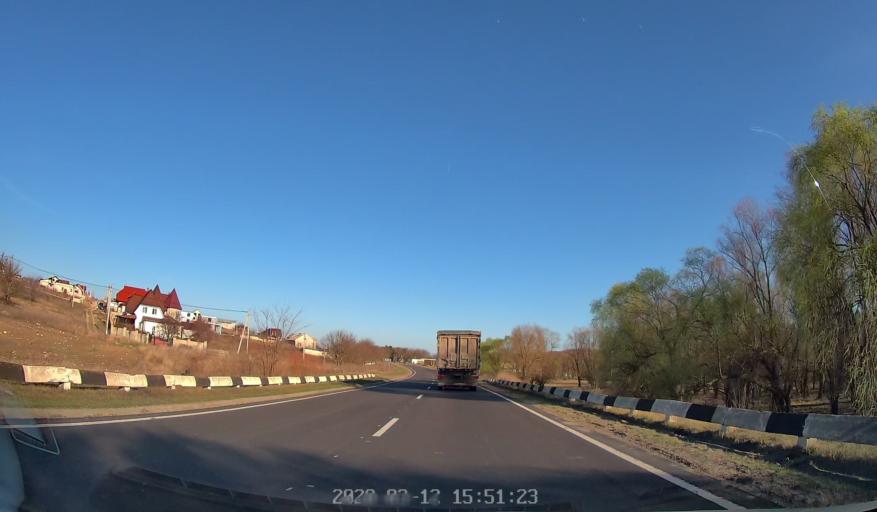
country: MD
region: Chisinau
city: Ciorescu
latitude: 47.0673
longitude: 28.9672
